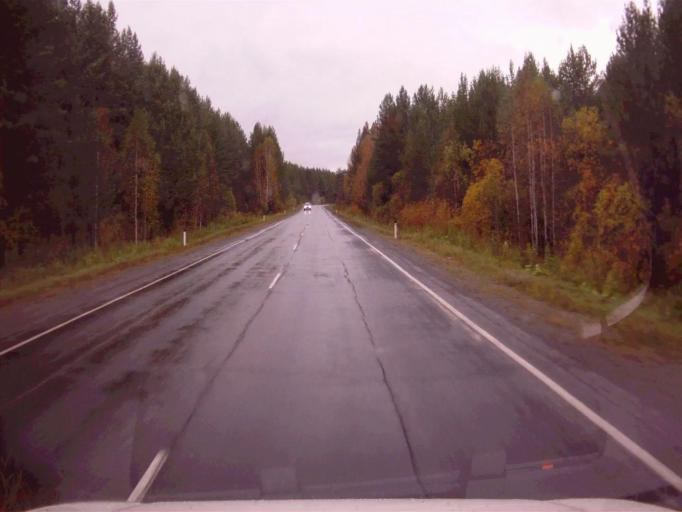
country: RU
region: Chelyabinsk
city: Verkhniy Ufaley
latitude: 56.0117
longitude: 60.3180
